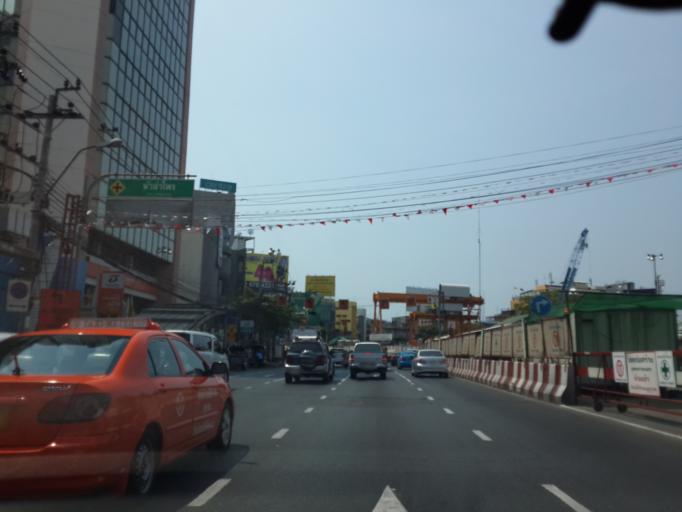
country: TH
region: Bangkok
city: Samphanthawong
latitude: 13.7374
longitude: 100.5172
